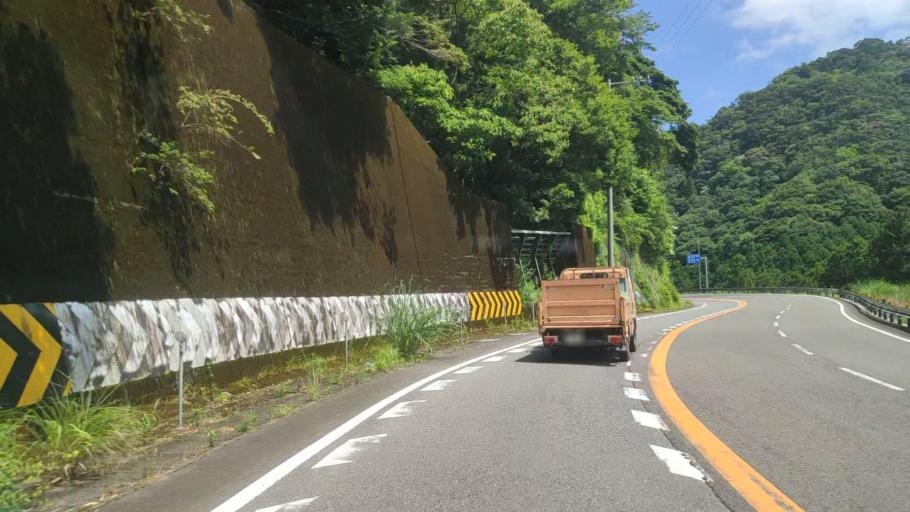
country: JP
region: Mie
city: Owase
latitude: 33.9224
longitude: 136.0960
